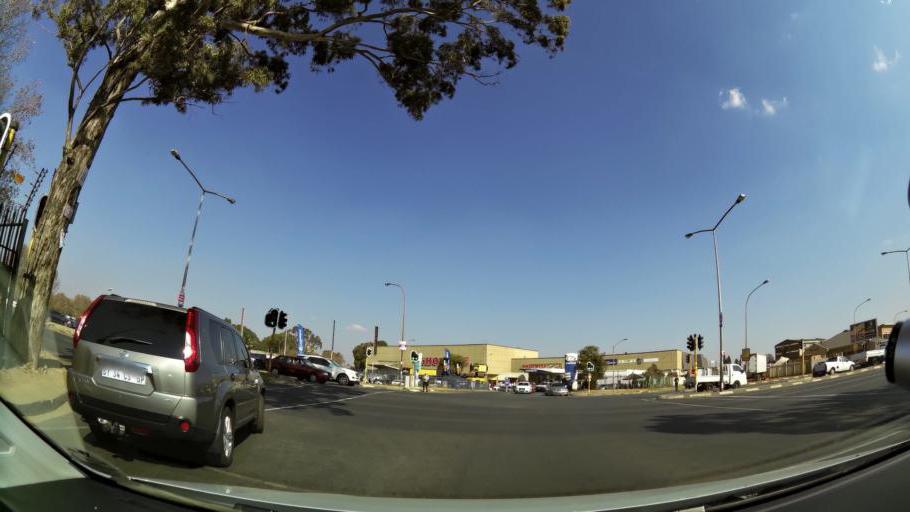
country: ZA
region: Gauteng
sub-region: City of Johannesburg Metropolitan Municipality
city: Modderfontein
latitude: -26.1069
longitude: 28.2374
